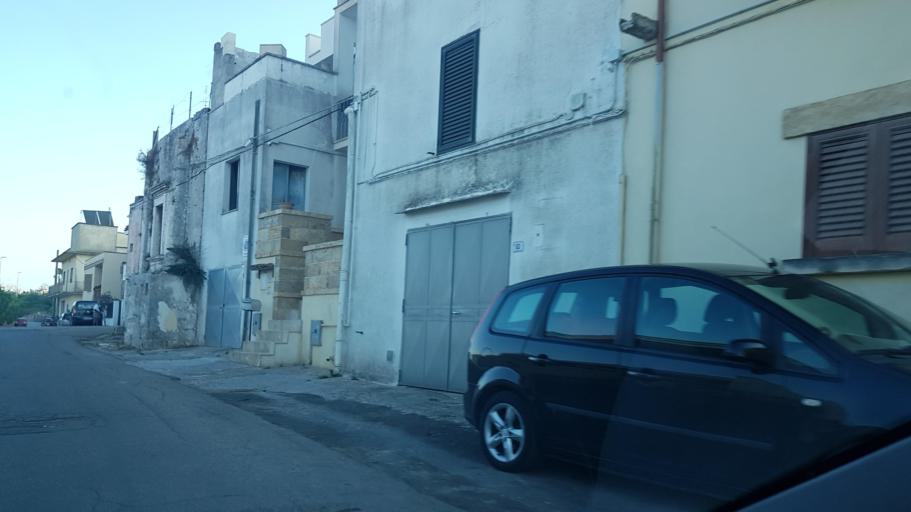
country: IT
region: Apulia
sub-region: Provincia di Lecce
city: Specchia
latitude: 39.9421
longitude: 18.3016
